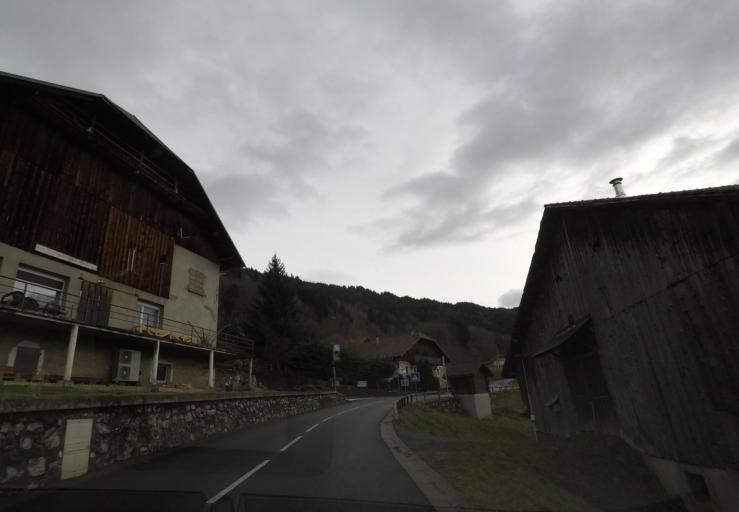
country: FR
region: Rhone-Alpes
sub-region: Departement de la Haute-Savoie
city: Araches-la-Frasse
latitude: 46.0718
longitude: 6.6154
